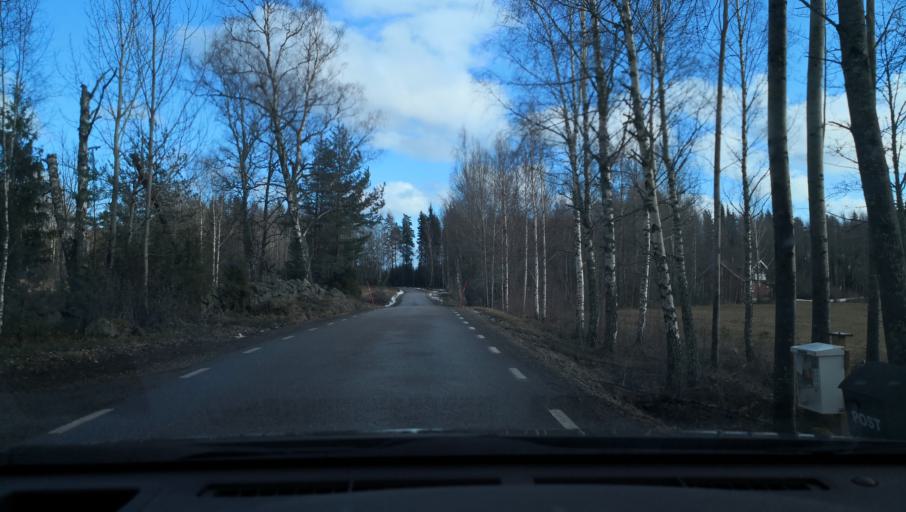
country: SE
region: Vaestmanland
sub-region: Arboga Kommun
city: Arboga
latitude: 59.3300
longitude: 15.7348
